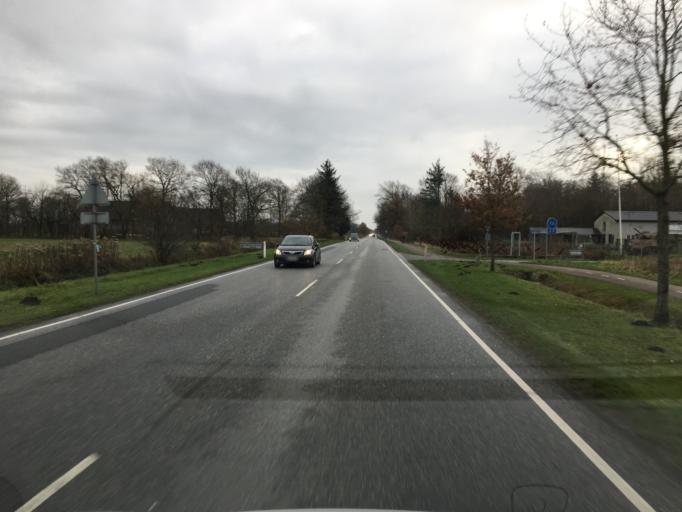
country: DK
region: South Denmark
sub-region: Tonder Kommune
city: Tonder
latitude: 54.9620
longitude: 8.8680
